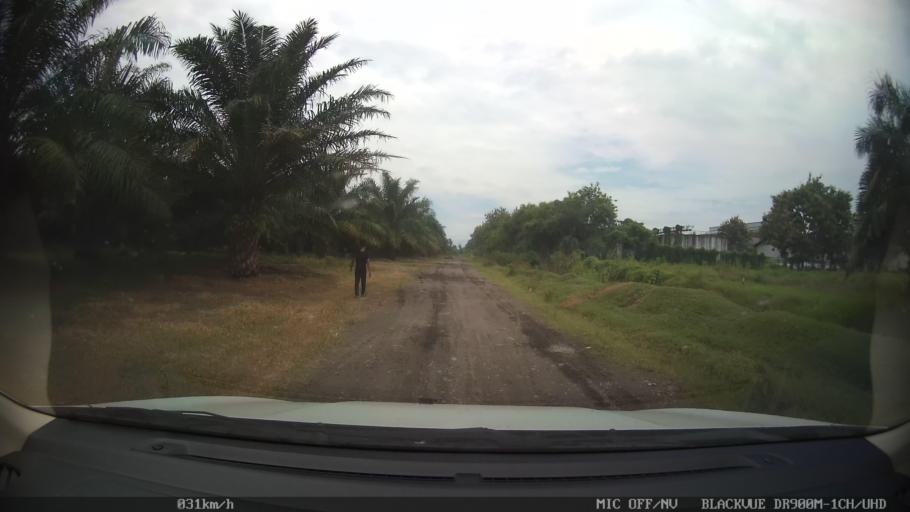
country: ID
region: North Sumatra
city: Sunggal
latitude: 3.6244
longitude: 98.5808
